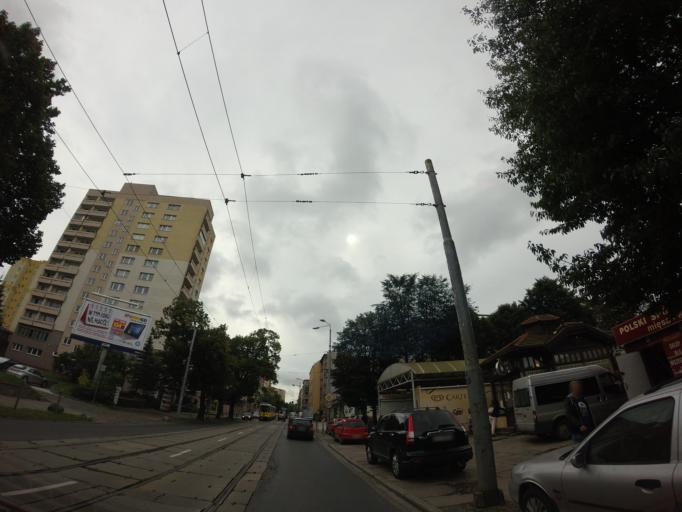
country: PL
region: West Pomeranian Voivodeship
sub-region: Szczecin
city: Szczecin
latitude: 53.4417
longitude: 14.5484
